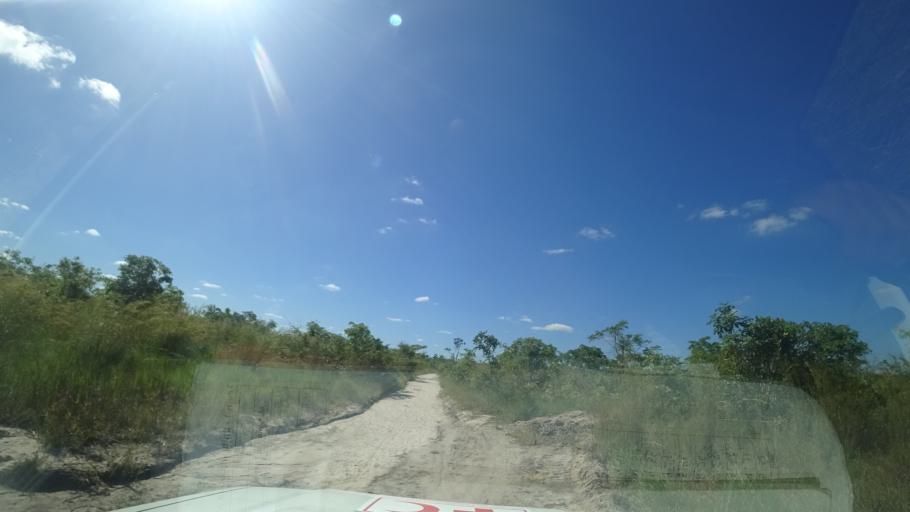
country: MZ
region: Sofala
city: Dondo
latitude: -19.4797
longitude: 34.6263
